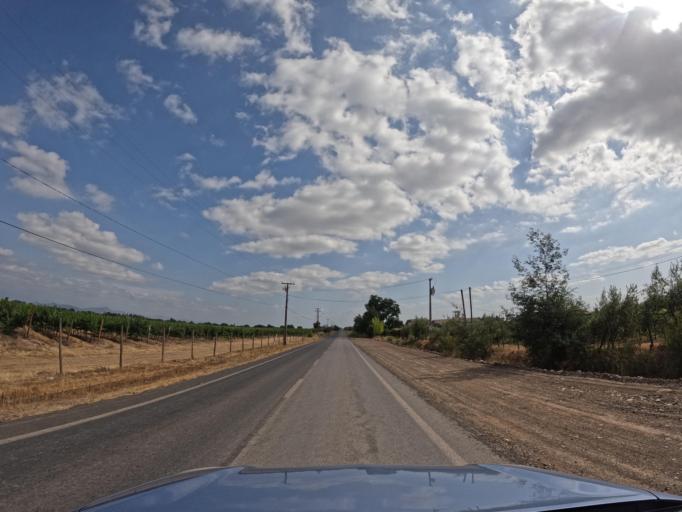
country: CL
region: Maule
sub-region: Provincia de Curico
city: Molina
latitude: -35.1732
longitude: -71.2925
